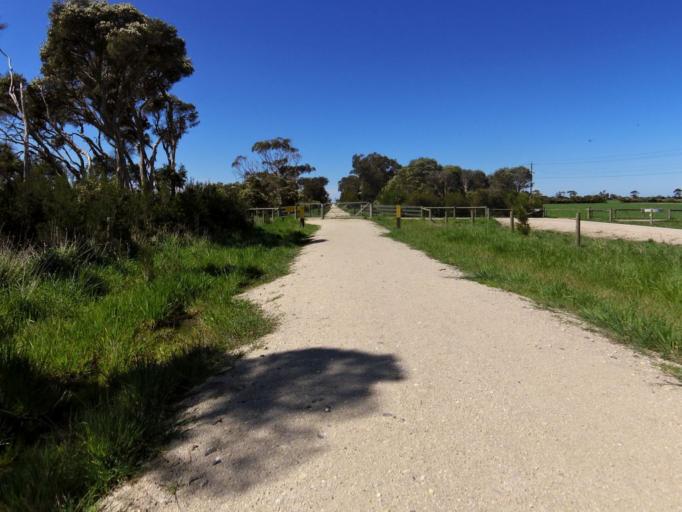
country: AU
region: Victoria
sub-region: Latrobe
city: Morwell
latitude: -38.6706
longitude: 146.3612
